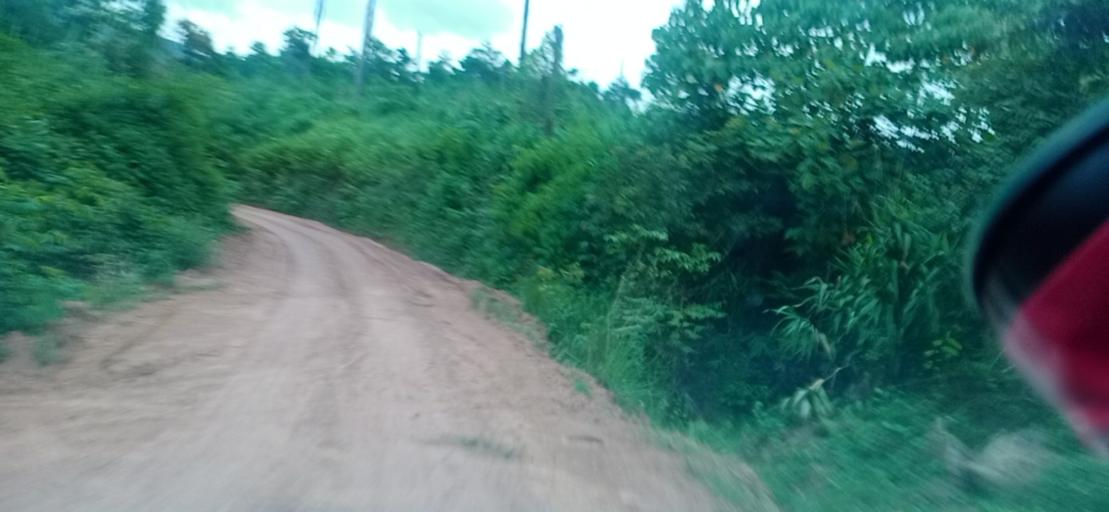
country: TH
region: Changwat Bueng Kan
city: Pak Khat
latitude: 18.5508
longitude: 103.4252
